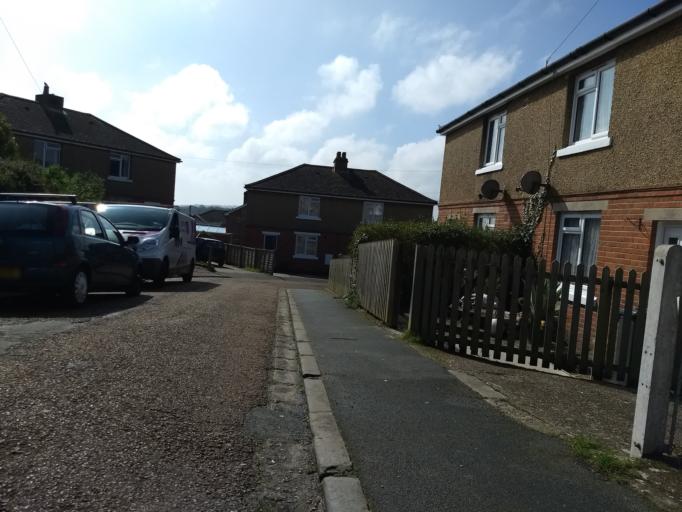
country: GB
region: England
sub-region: Isle of Wight
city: Ryde
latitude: 50.7186
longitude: -1.1701
